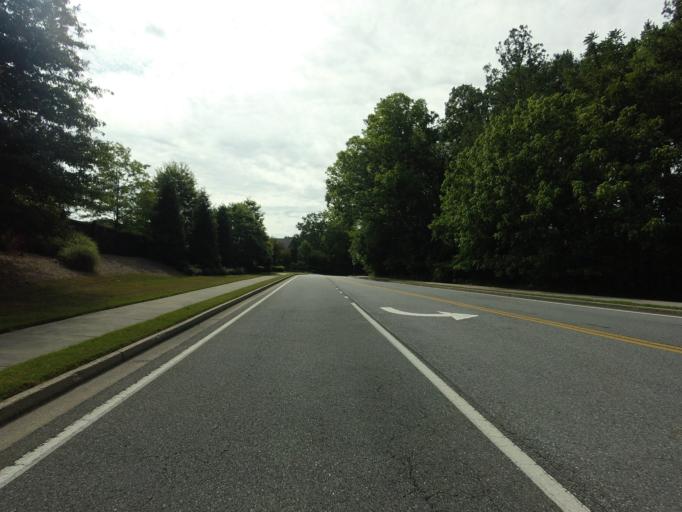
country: US
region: Georgia
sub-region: Fulton County
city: Johns Creek
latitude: 34.0644
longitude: -84.1849
